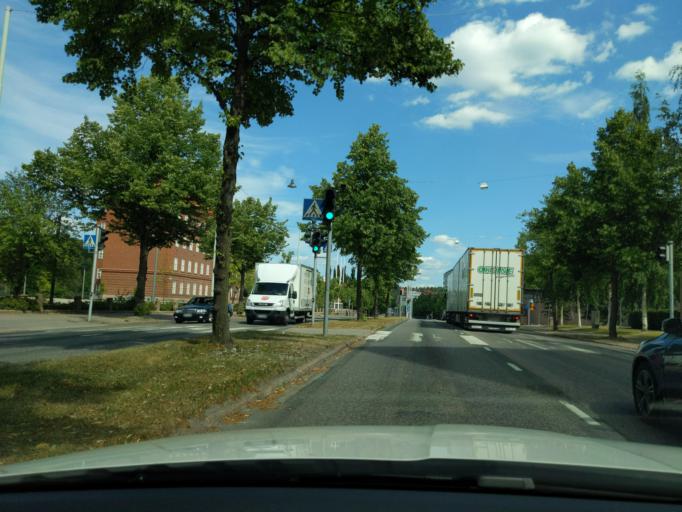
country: FI
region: Paijanne Tavastia
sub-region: Lahti
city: Lahti
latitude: 60.9854
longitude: 25.6531
